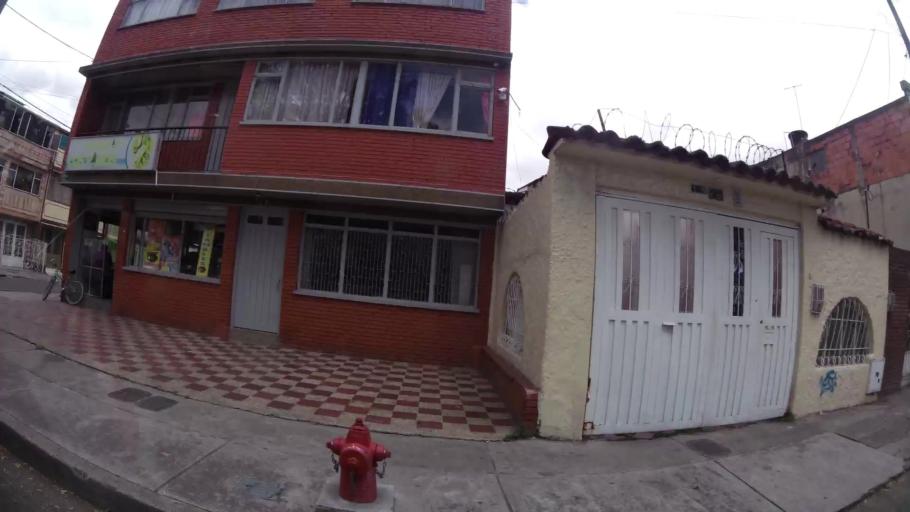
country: CO
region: Bogota D.C.
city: Bogota
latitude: 4.6004
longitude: -74.1082
